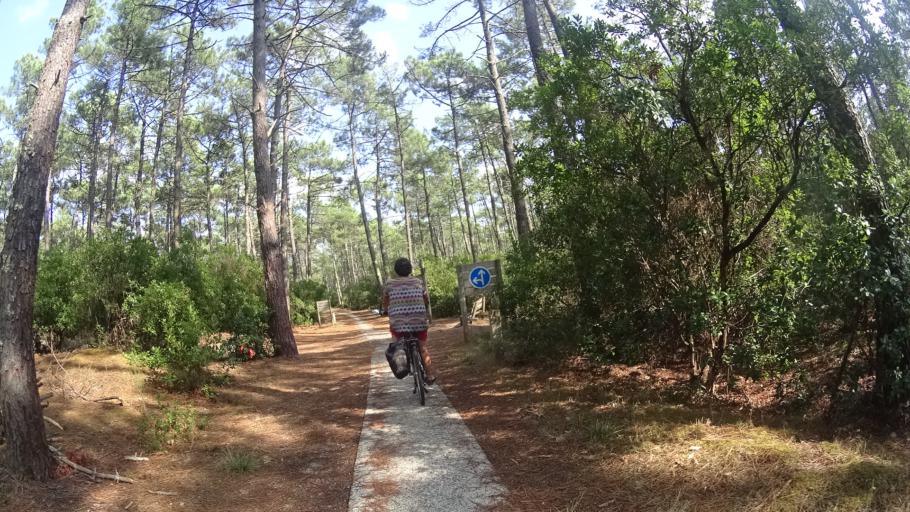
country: FR
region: Aquitaine
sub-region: Departement de la Gironde
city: Lacanau
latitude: 44.9633
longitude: -1.1728
